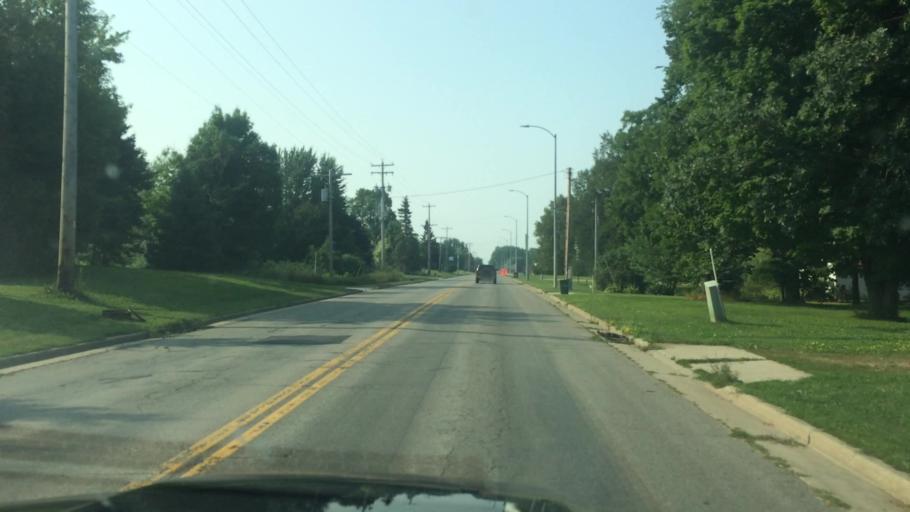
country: US
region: Wisconsin
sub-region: Marathon County
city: Stratford
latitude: 44.8126
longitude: -90.0792
